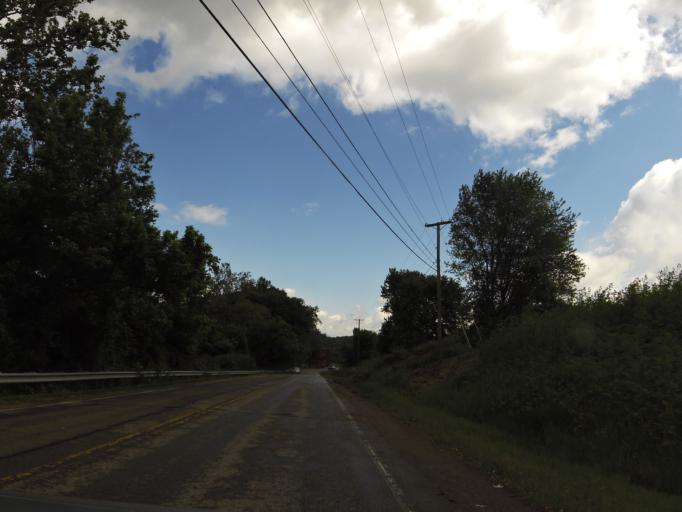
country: US
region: Ohio
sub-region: Athens County
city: Athens
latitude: 39.3273
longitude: -82.0882
